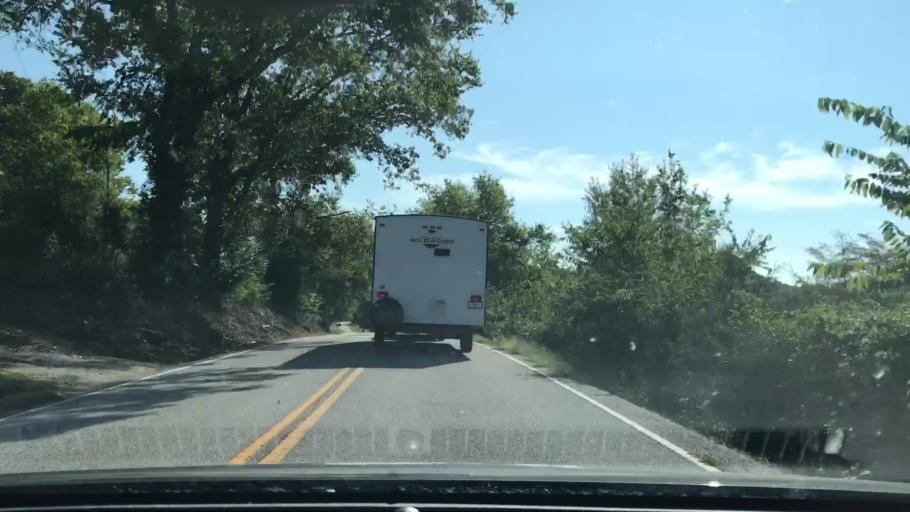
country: US
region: Tennessee
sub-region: Smith County
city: Carthage
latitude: 36.3477
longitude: -85.8727
